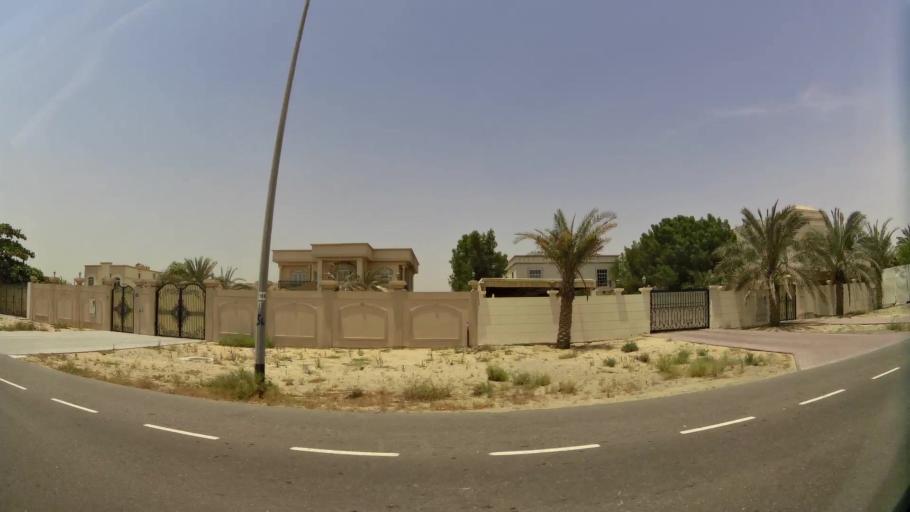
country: AE
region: Ash Shariqah
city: Sharjah
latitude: 25.2476
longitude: 55.4669
